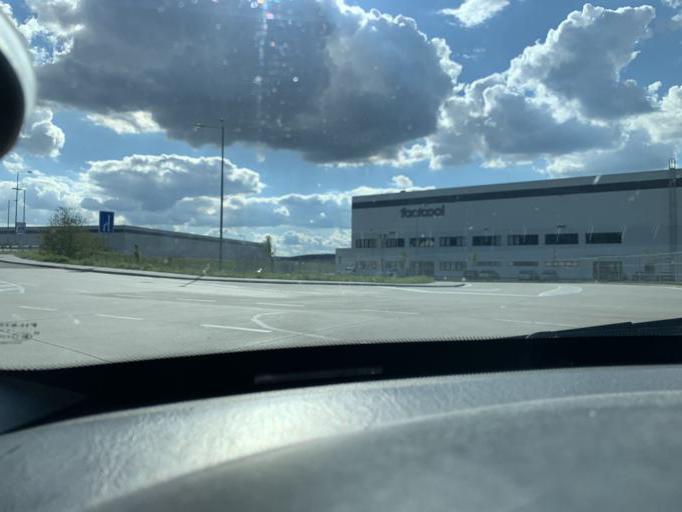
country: SK
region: Trenciansky
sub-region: Okres Nove Mesto nad Vahom
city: Nove Mesto nad Vahom
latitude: 48.7655
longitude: 17.8783
